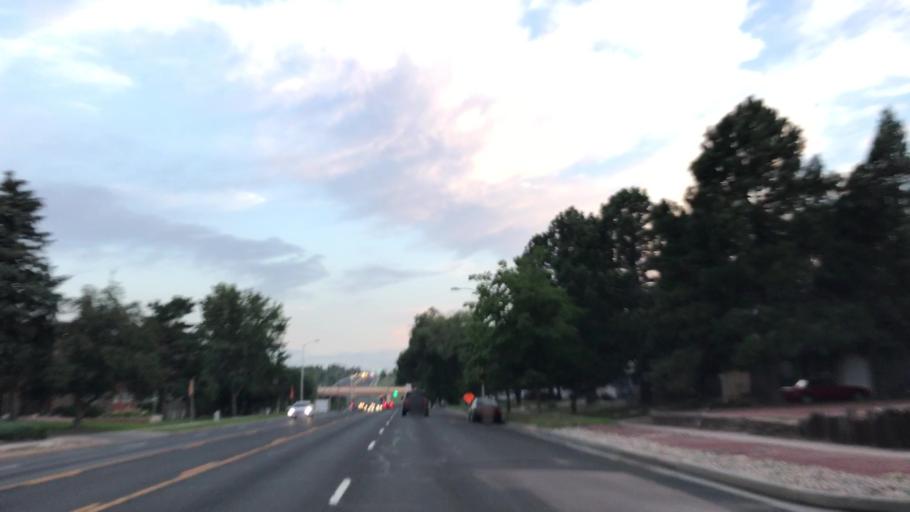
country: US
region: Colorado
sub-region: El Paso County
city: Colorado Springs
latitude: 38.8209
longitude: -104.7806
